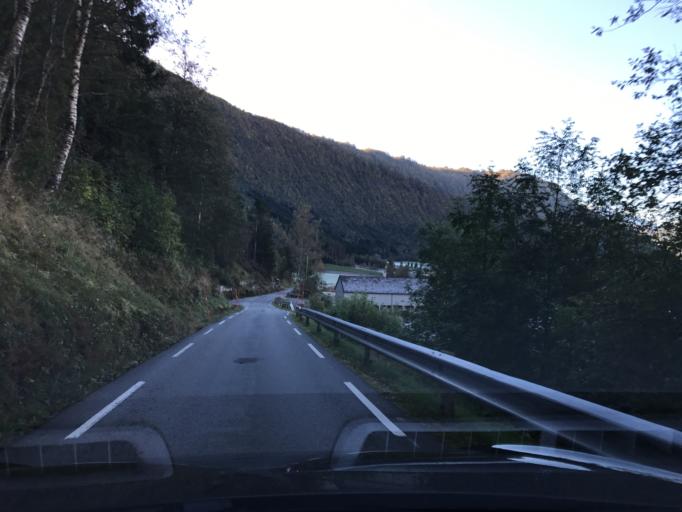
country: NO
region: More og Romsdal
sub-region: Norddal
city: Valldal
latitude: 62.3251
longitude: 7.3321
